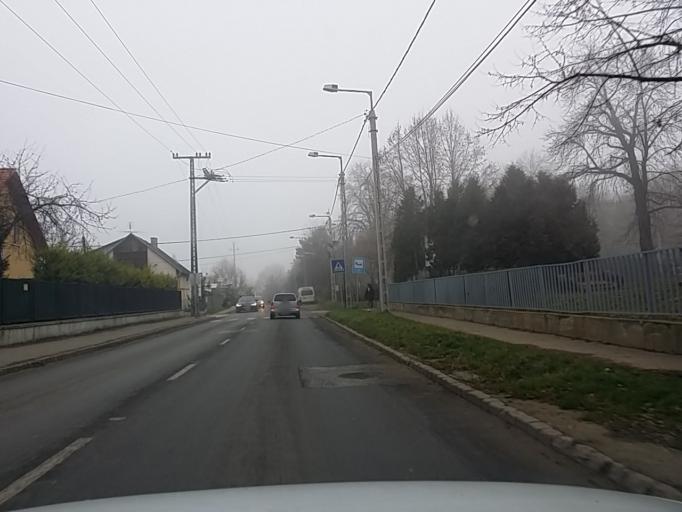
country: HU
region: Pest
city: Budakeszi
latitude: 47.5126
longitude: 18.9264
